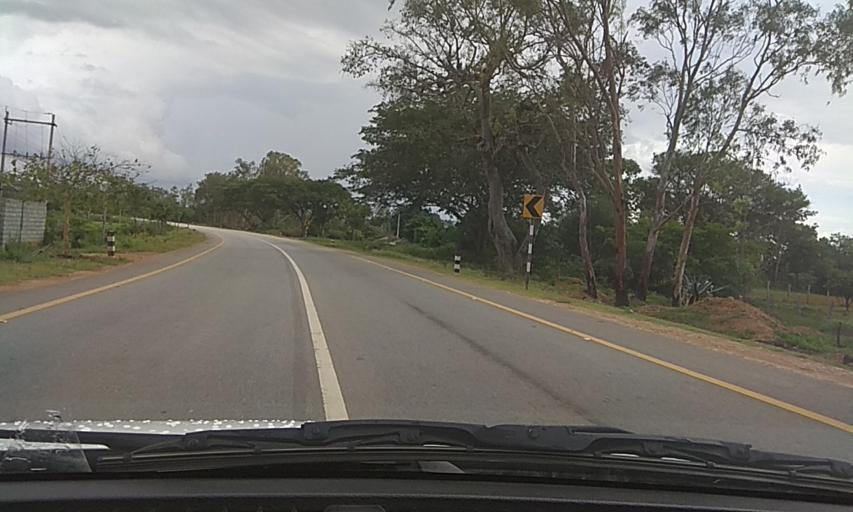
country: IN
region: Karnataka
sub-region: Tumkur
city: Kunigal
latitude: 12.9155
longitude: 77.0321
